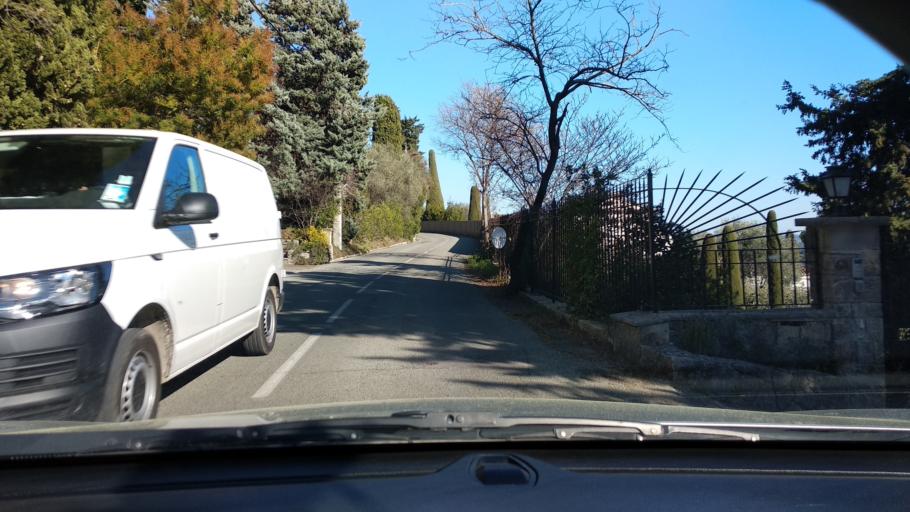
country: FR
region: Provence-Alpes-Cote d'Azur
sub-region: Departement des Alpes-Maritimes
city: Peymeinade
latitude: 43.6473
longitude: 6.8945
